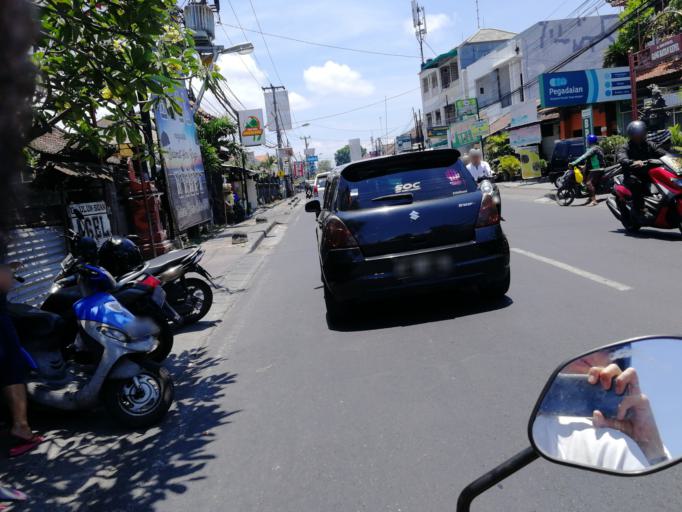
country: ID
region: Bali
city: Karyadharma
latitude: -8.6868
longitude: 115.1932
